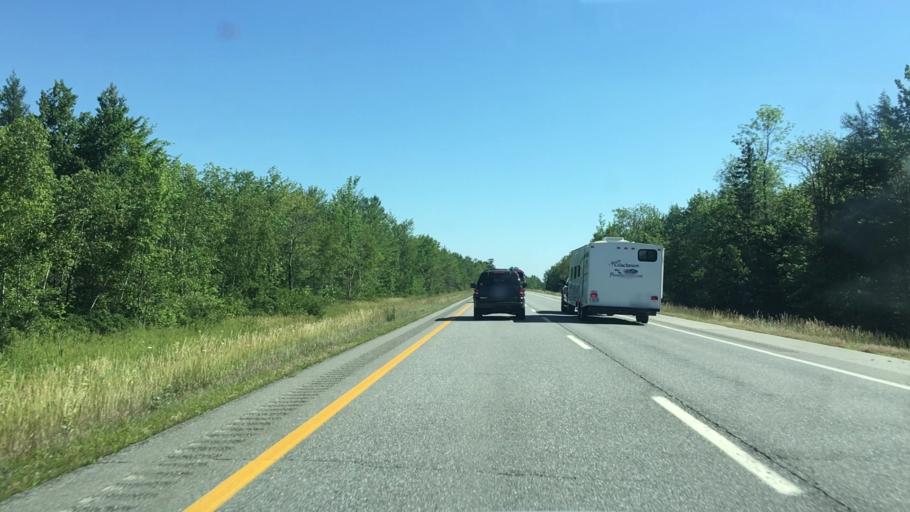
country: US
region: Maine
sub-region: Waldo County
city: Burnham
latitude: 44.6895
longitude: -69.4712
